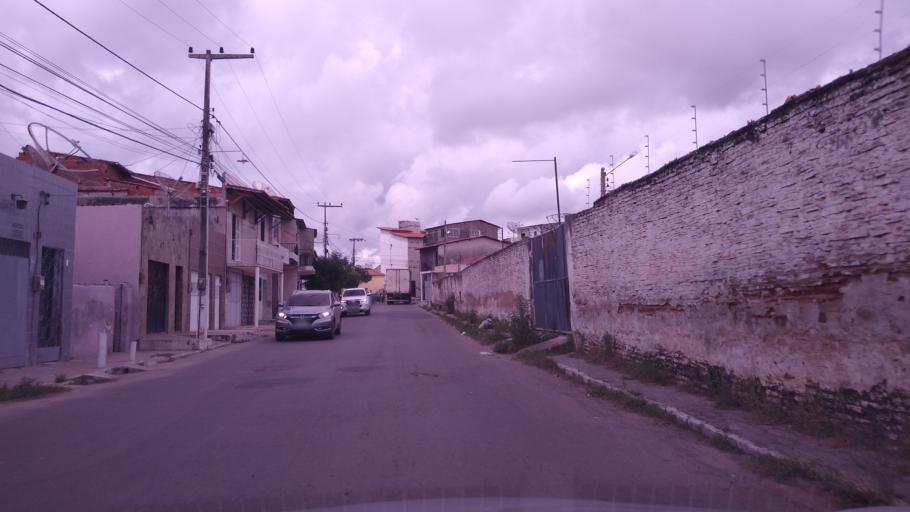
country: BR
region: Ceara
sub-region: Quixada
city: Quixada
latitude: -4.9645
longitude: -39.0149
